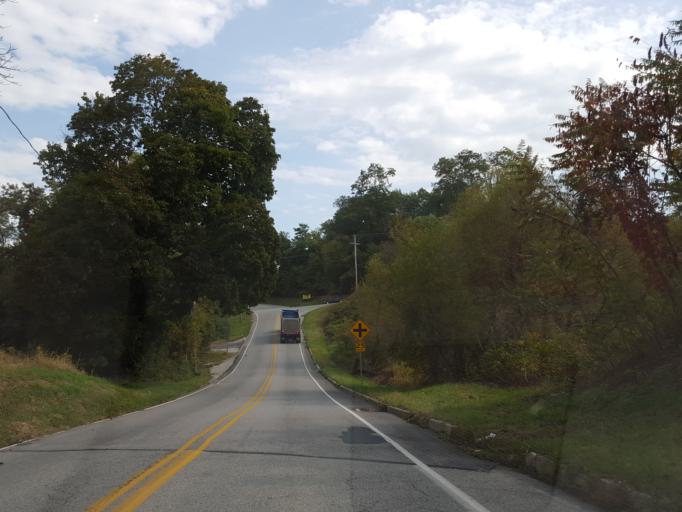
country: US
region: Pennsylvania
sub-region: York County
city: Yoe
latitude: 39.9104
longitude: -76.6476
